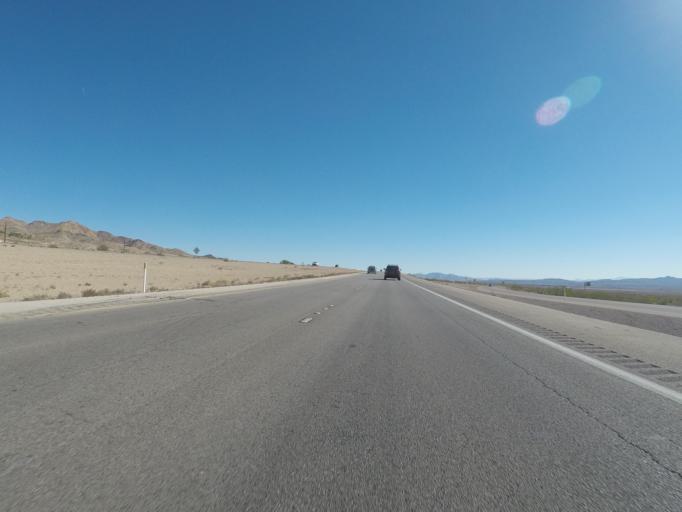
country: US
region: Nevada
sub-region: Clark County
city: Boulder City
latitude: 35.9675
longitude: -114.8984
